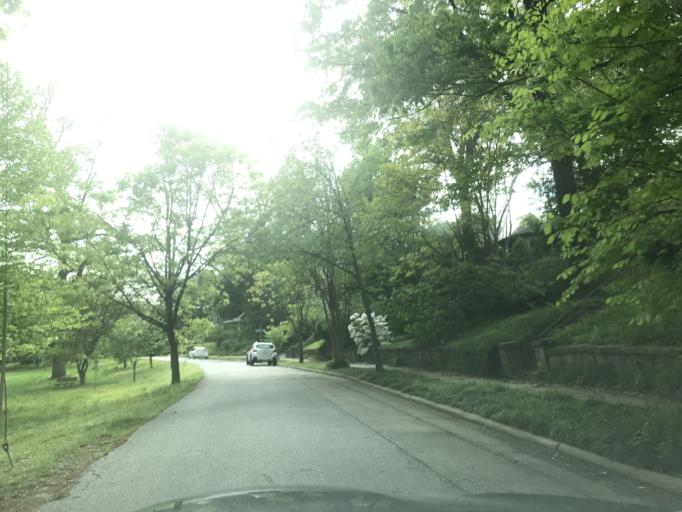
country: US
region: North Carolina
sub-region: Wake County
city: West Raleigh
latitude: 35.7858
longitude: -78.6537
